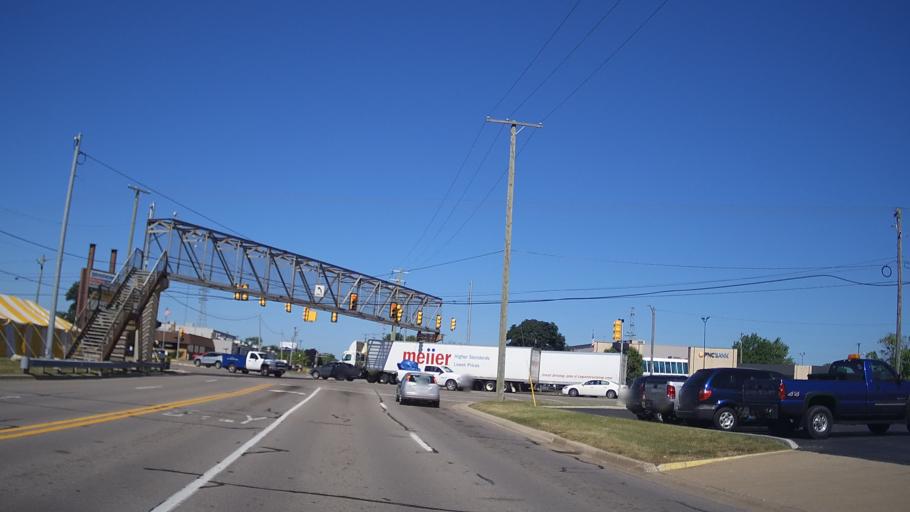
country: US
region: Michigan
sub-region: Macomb County
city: Fraser
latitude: 42.5317
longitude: -82.9399
